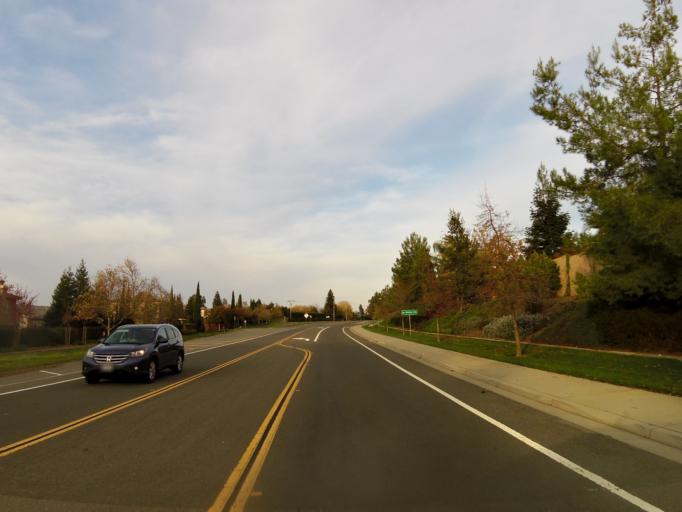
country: US
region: California
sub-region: El Dorado County
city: El Dorado Hills
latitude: 38.6388
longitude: -121.0758
